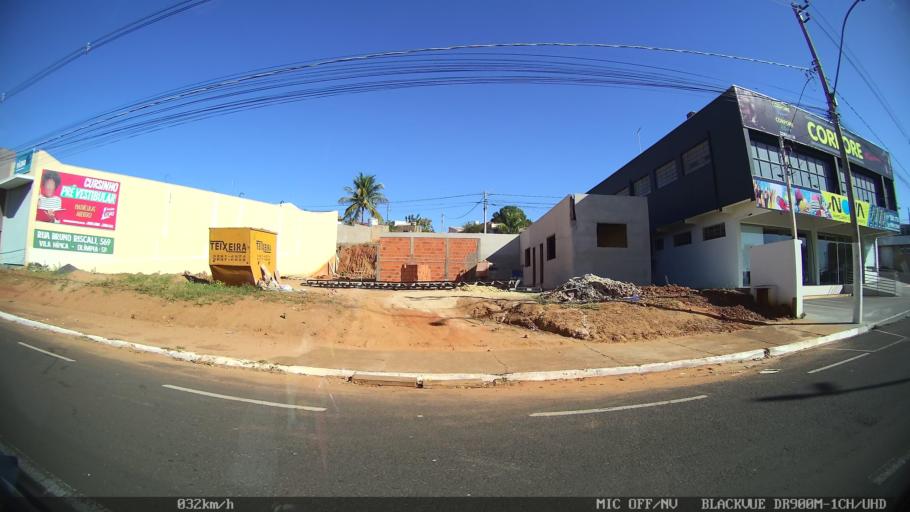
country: BR
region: Sao Paulo
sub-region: Olimpia
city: Olimpia
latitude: -20.7422
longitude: -48.9095
